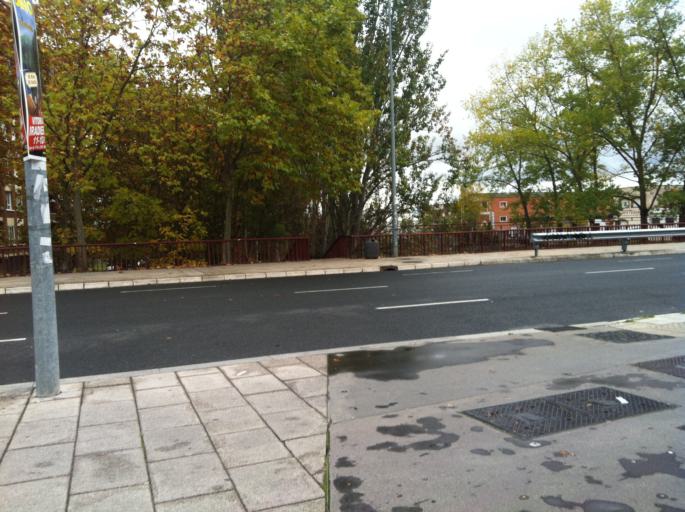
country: ES
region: Basque Country
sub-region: Provincia de Alava
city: Gasteiz / Vitoria
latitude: 42.8405
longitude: -2.6638
